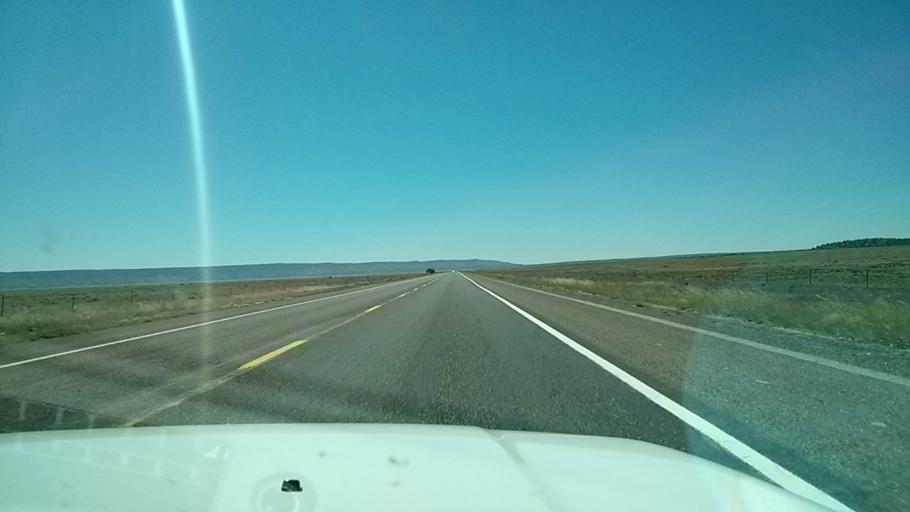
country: US
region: Arizona
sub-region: Mohave County
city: Peach Springs
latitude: 35.4585
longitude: -113.1067
